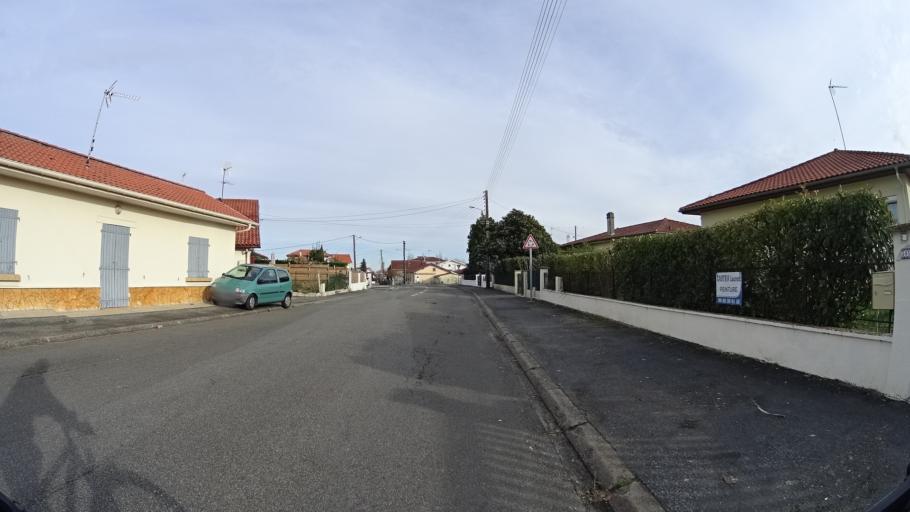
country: FR
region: Aquitaine
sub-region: Departement des Landes
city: Saint-Paul-les-Dax
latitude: 43.7309
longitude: -1.0525
